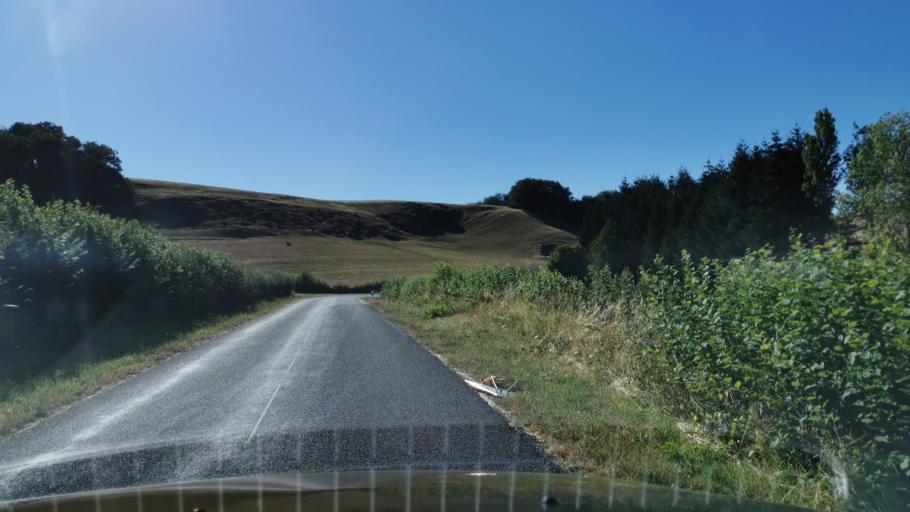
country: FR
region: Bourgogne
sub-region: Departement de Saone-et-Loire
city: Montcenis
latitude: 46.8001
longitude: 4.3611
